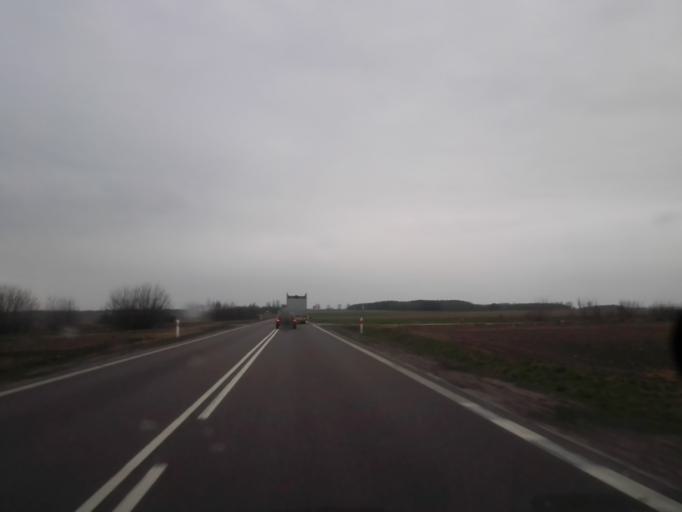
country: PL
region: Podlasie
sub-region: Powiat grajewski
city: Grajewo
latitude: 53.6125
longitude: 22.3812
